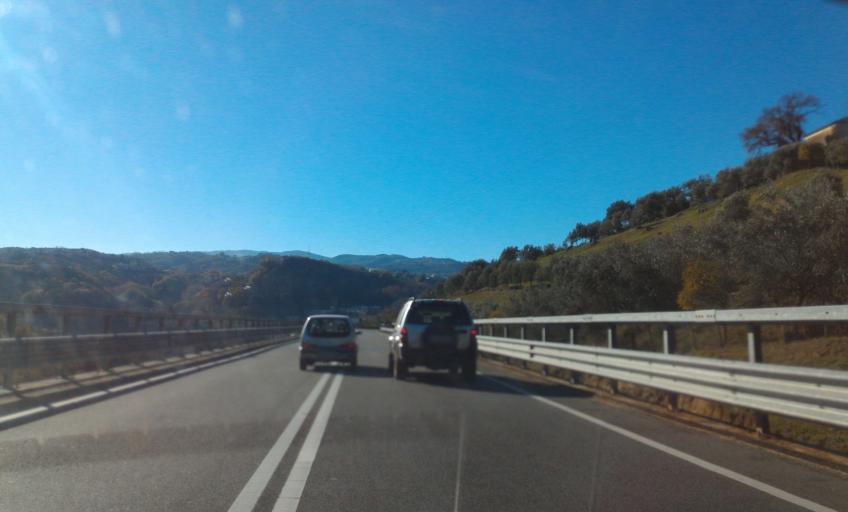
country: IT
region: Calabria
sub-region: Provincia di Cosenza
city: Cosenza
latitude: 39.2943
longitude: 16.2652
